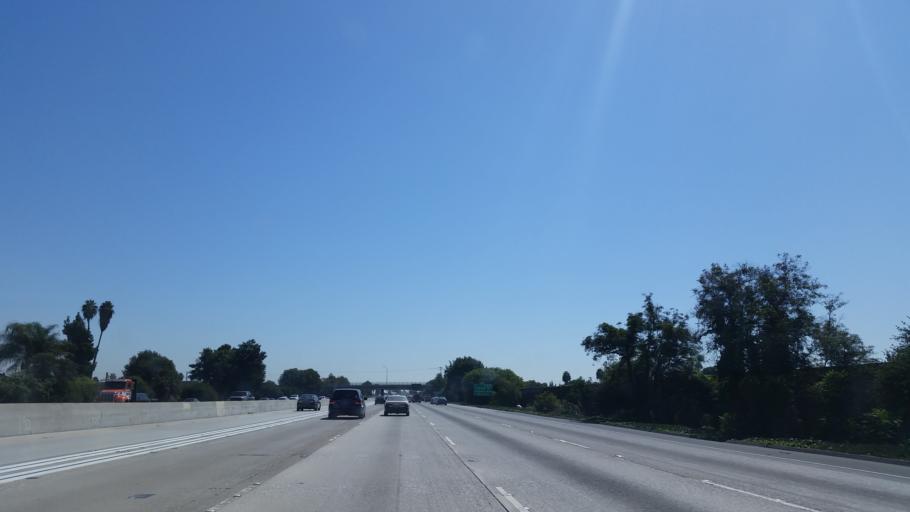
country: US
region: California
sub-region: Los Angeles County
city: Hawaiian Gardens
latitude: 33.8420
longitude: -118.0903
